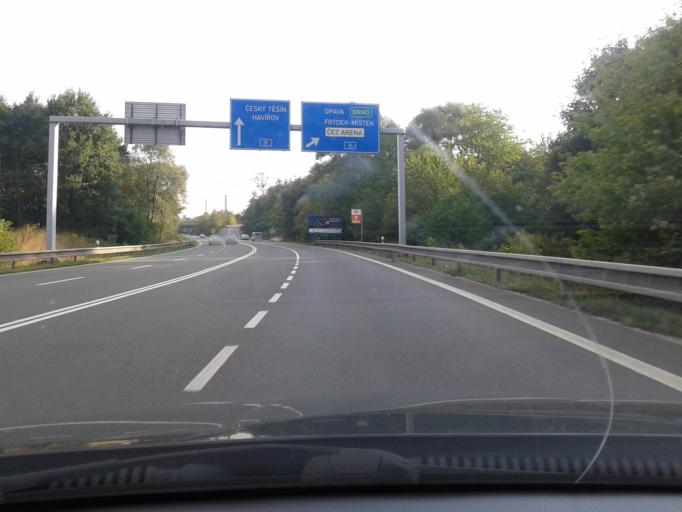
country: CZ
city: Vratimov
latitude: 49.8101
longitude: 18.3314
